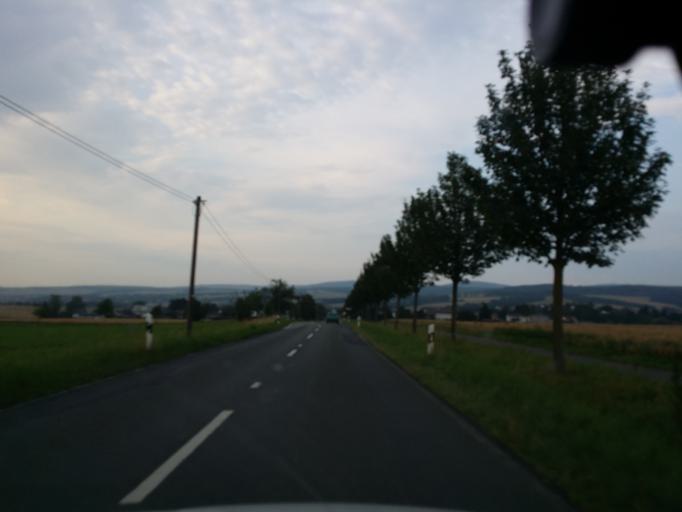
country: DE
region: Hesse
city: Bad Camberg
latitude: 50.2614
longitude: 8.2736
